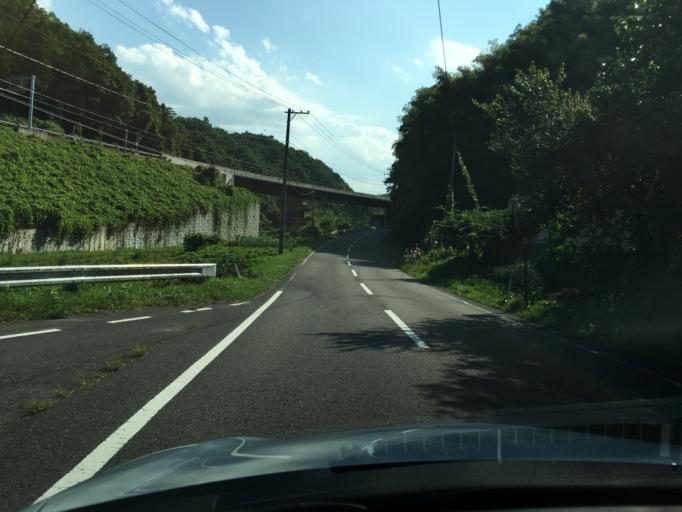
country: JP
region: Fukushima
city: Ishikawa
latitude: 37.2059
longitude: 140.5191
